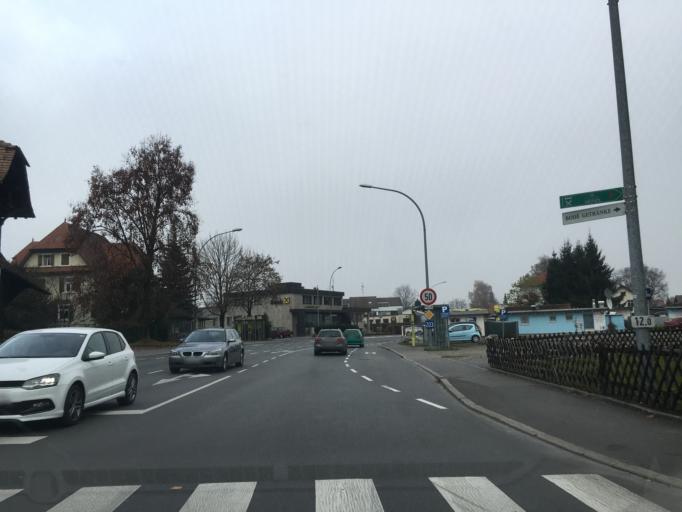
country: AT
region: Vorarlberg
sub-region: Politischer Bezirk Dornbirn
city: Lustenau
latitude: 47.4375
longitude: 9.6563
